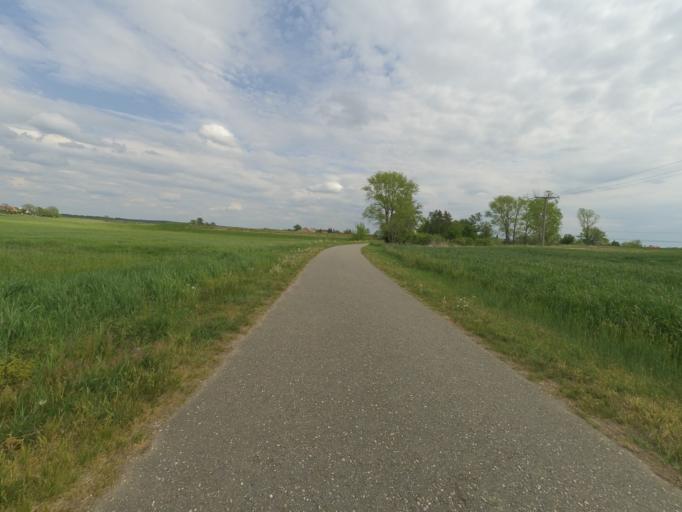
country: DE
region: Saxony
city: Strehla
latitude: 51.3459
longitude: 13.2573
